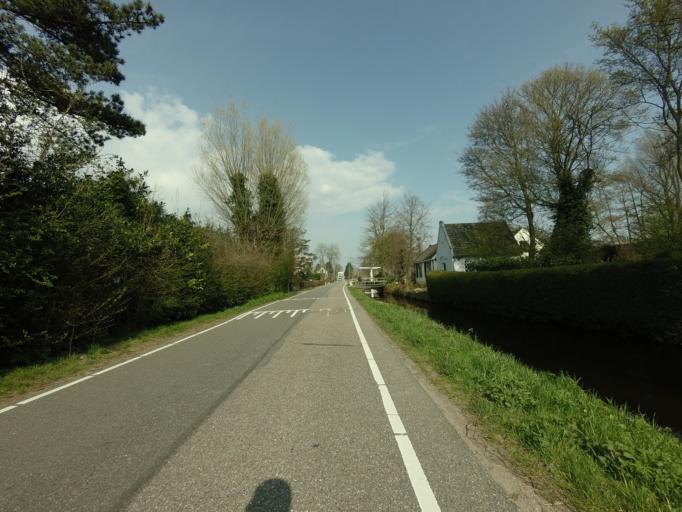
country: NL
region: North Holland
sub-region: Gemeente Wijdemeren
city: Kortenhoef
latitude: 52.2728
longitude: 5.1056
